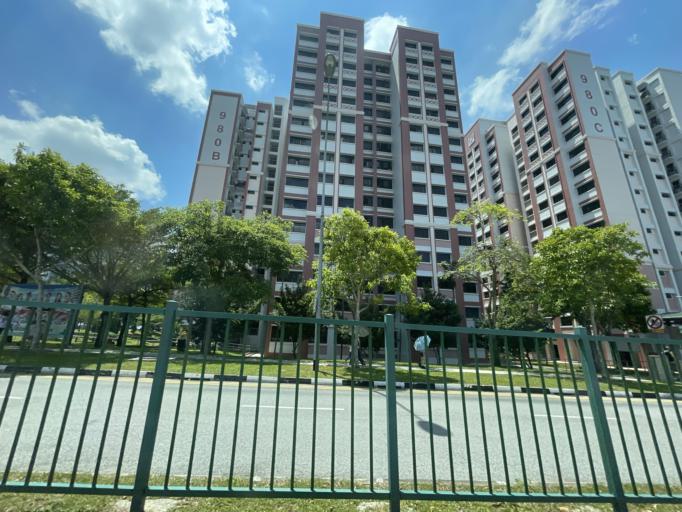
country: MY
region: Johor
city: Kampung Pasir Gudang Baru
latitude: 1.3797
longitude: 103.8815
